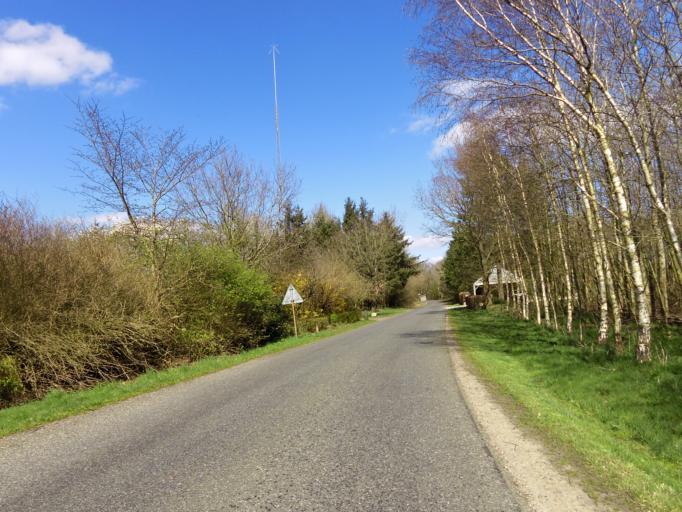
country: DK
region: South Denmark
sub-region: Esbjerg Kommune
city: Ribe
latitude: 55.3463
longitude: 8.8354
